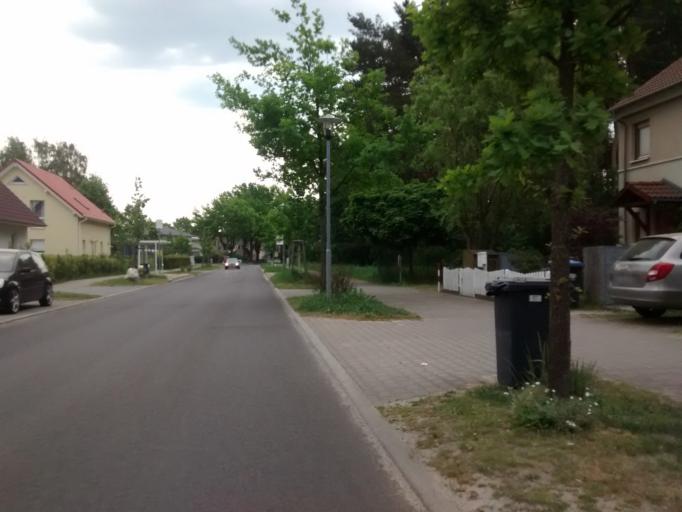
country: DE
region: Brandenburg
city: Hohen Neuendorf
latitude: 52.6689
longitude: 13.2651
